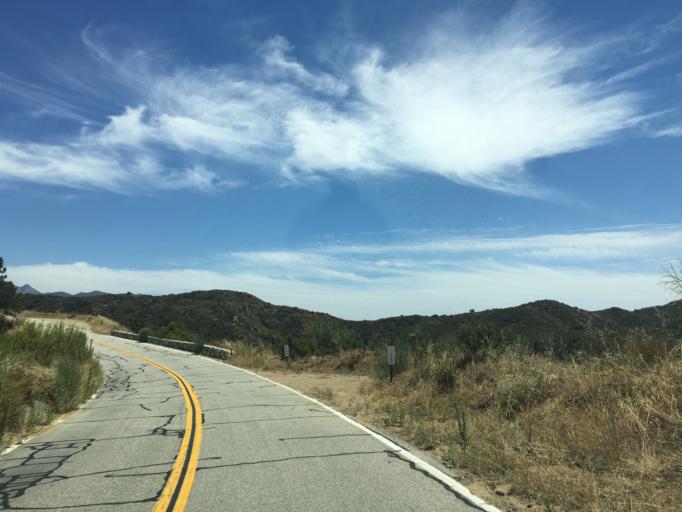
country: US
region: California
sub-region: Los Angeles County
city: Glendora
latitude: 34.1995
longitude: -117.8294
